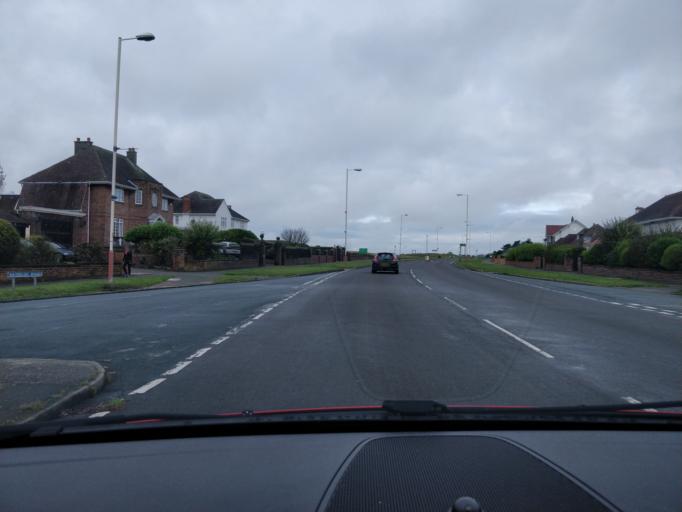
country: GB
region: England
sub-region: Sefton
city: Southport
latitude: 53.6234
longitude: -3.0264
